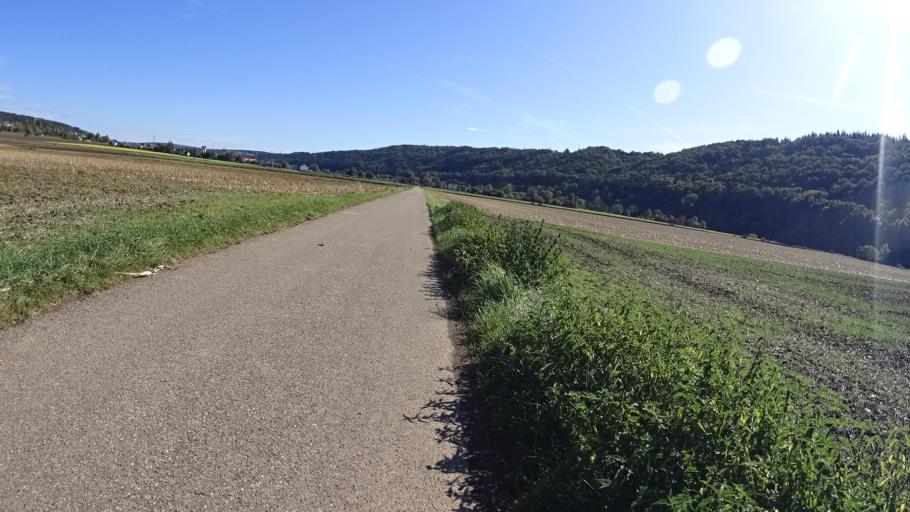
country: DE
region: Bavaria
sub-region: Upper Bavaria
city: Eichstaett
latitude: 48.8764
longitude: 11.2226
